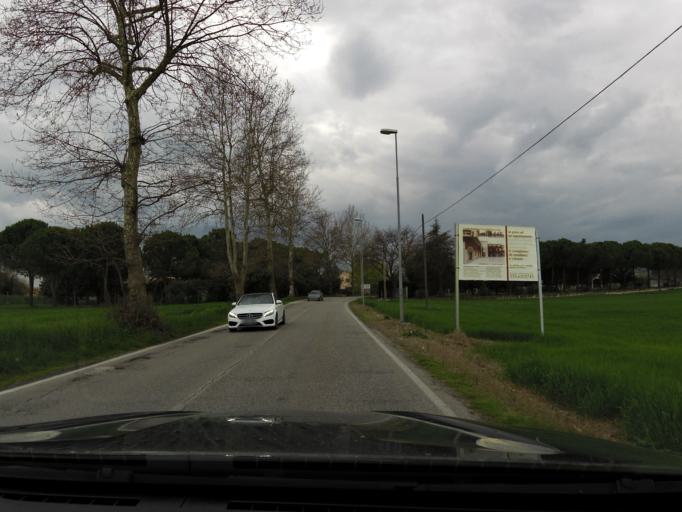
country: IT
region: The Marches
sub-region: Provincia di Ancona
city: Loreto Stazione
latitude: 43.4460
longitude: 13.6120
